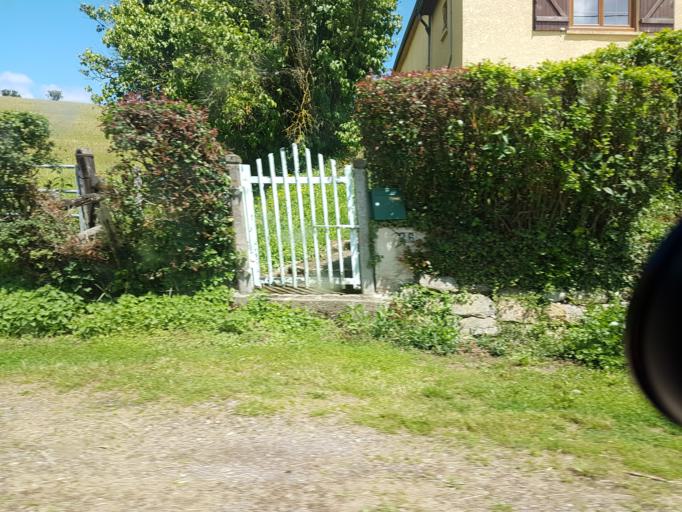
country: FR
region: Bourgogne
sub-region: Departement de Saone-et-Loire
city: Curgy
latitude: 47.0198
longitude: 4.4373
